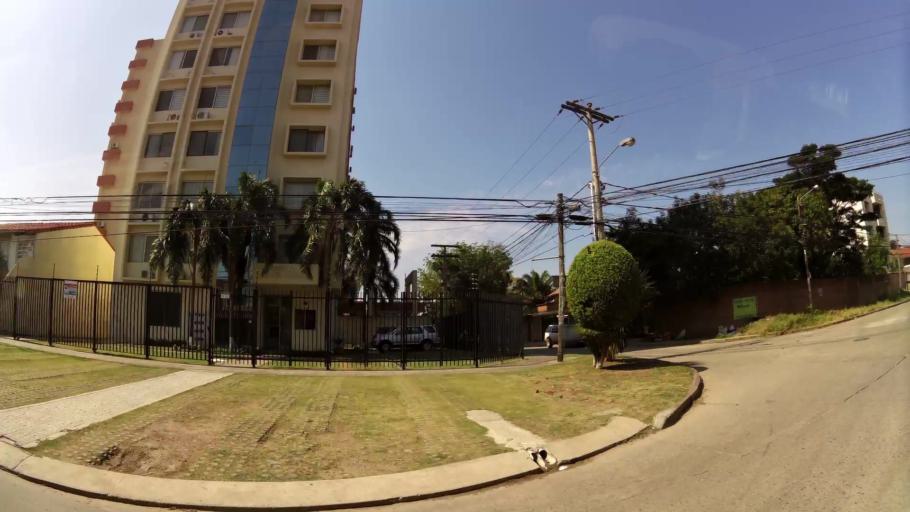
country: BO
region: Santa Cruz
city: Santa Cruz de la Sierra
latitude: -17.7445
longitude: -63.1693
